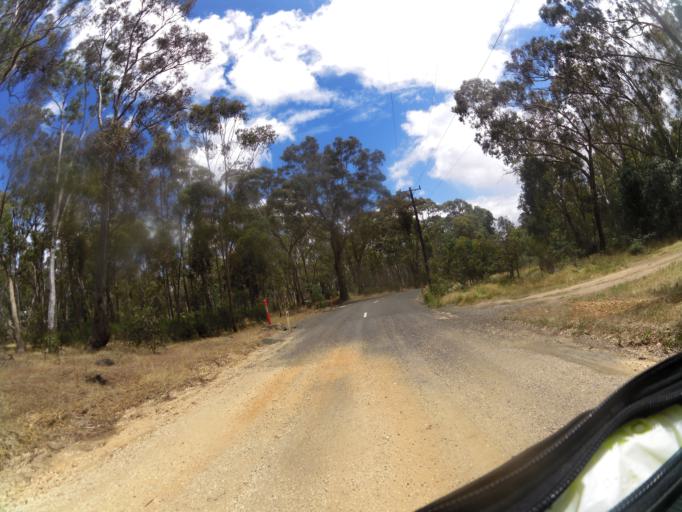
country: AU
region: Victoria
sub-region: Mount Alexander
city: Castlemaine
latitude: -37.0311
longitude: 144.2471
